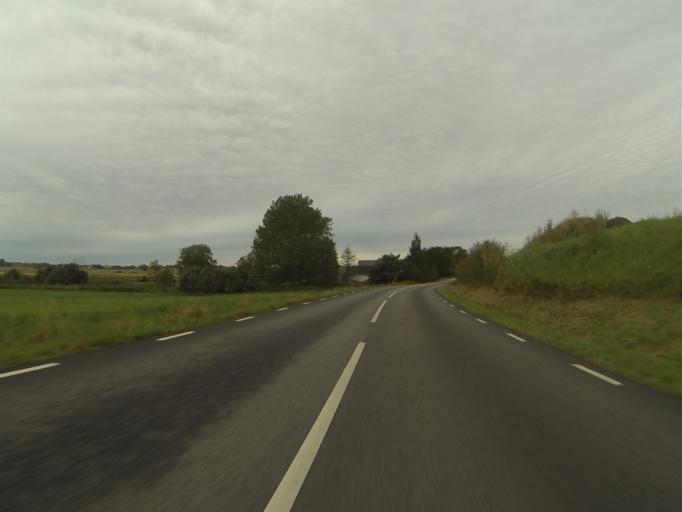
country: SE
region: Skane
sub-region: Staffanstorps Kommun
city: Staffanstorp
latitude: 55.6231
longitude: 13.1924
